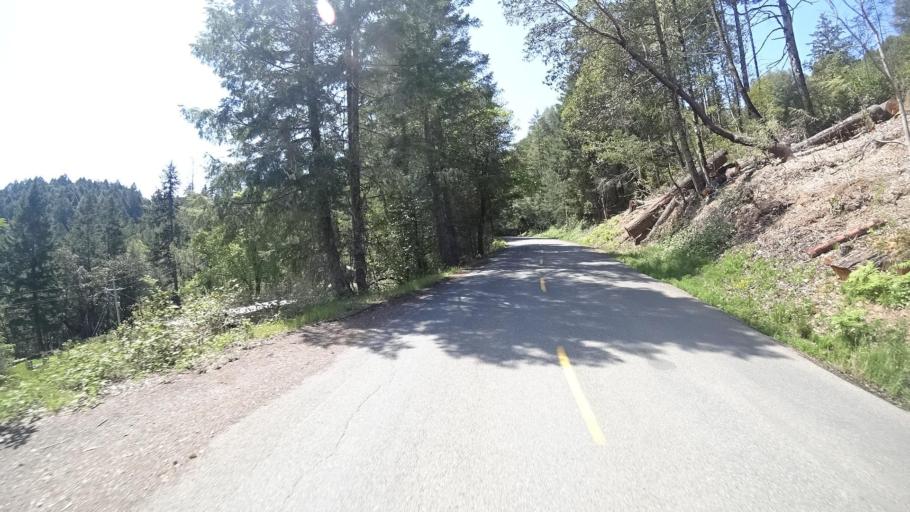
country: US
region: California
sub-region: Humboldt County
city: Redway
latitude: 40.1410
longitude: -123.6296
